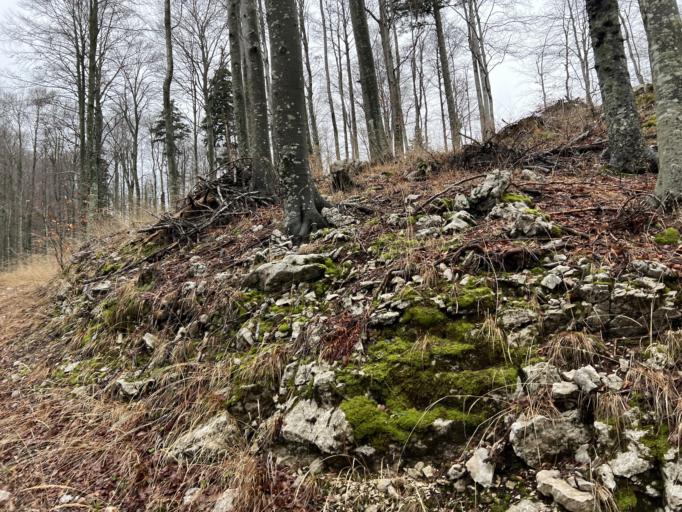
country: SI
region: Ajdovscina
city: Lokavec
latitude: 45.9517
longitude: 13.8206
